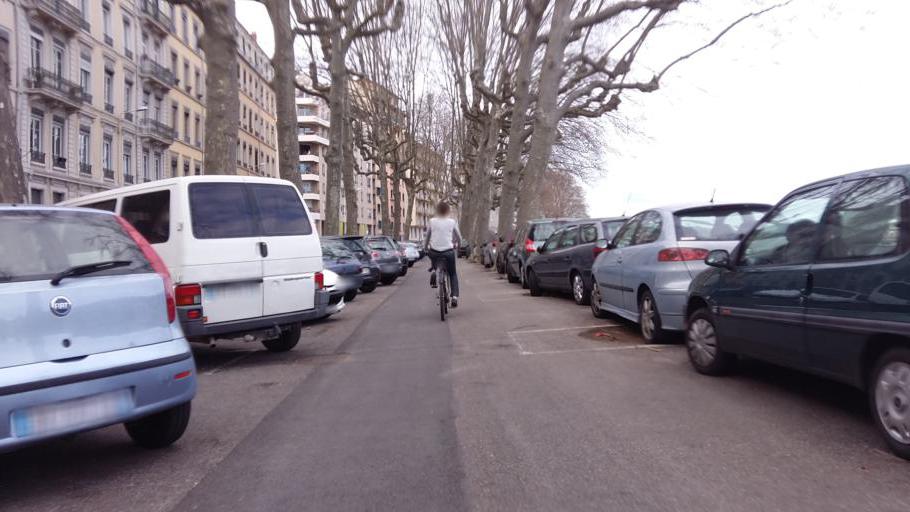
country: FR
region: Rhone-Alpes
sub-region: Departement du Rhone
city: Tassin-la-Demi-Lune
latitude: 45.7775
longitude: 4.8079
